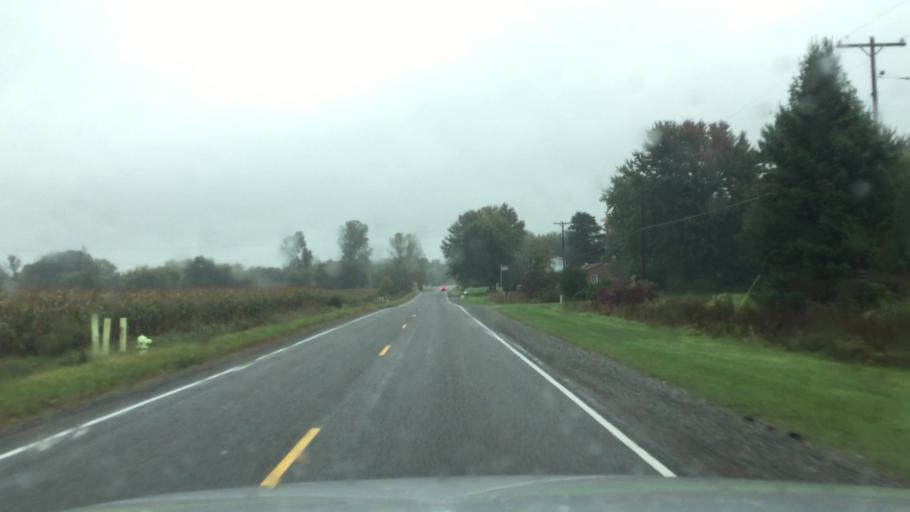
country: US
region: Michigan
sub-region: Saginaw County
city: Bridgeport
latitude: 43.3215
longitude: -83.8296
